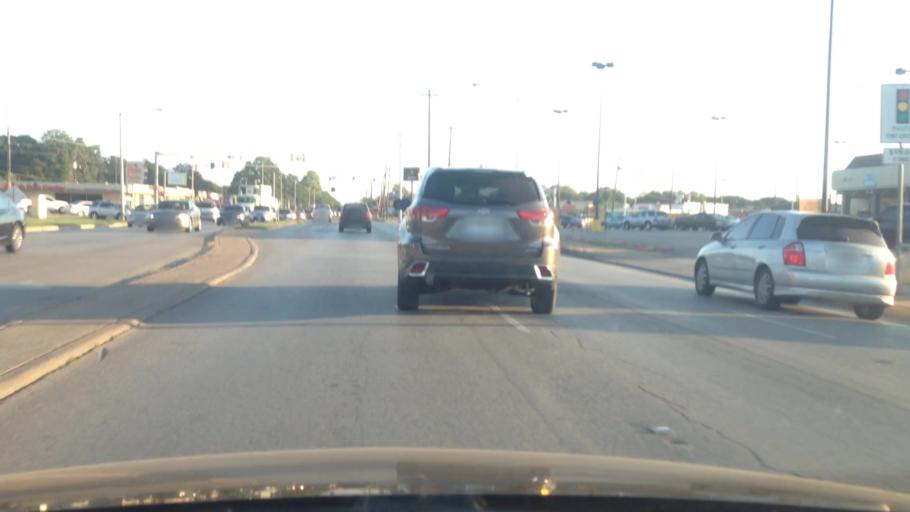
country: US
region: Texas
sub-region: Tarrant County
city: Haltom City
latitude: 32.7798
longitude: -97.2907
